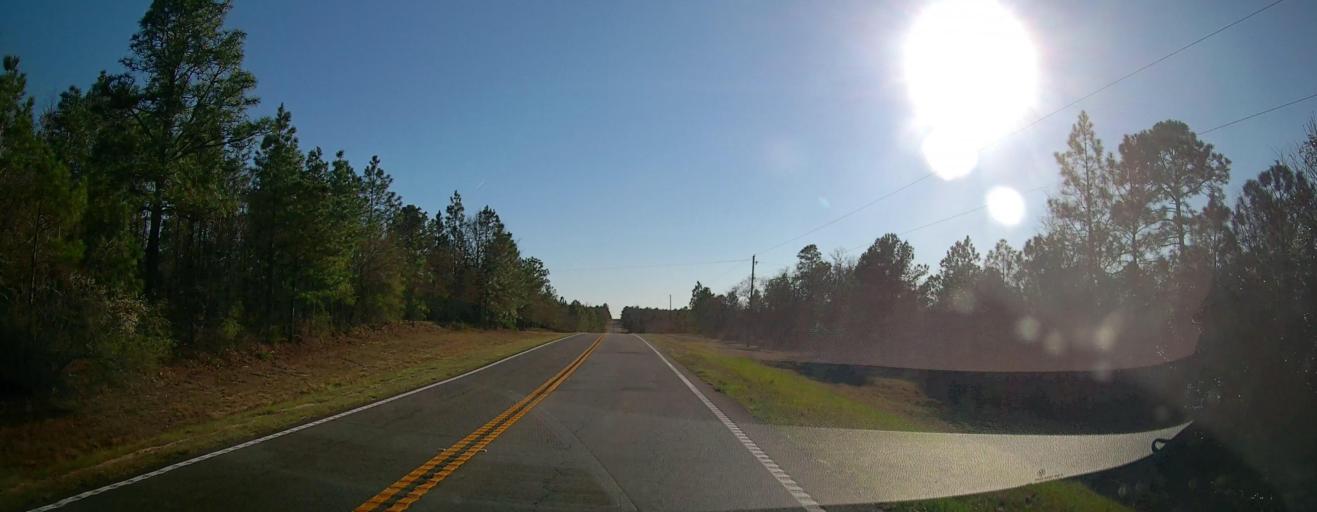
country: US
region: Georgia
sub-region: Taylor County
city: Butler
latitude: 32.5481
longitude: -84.2803
